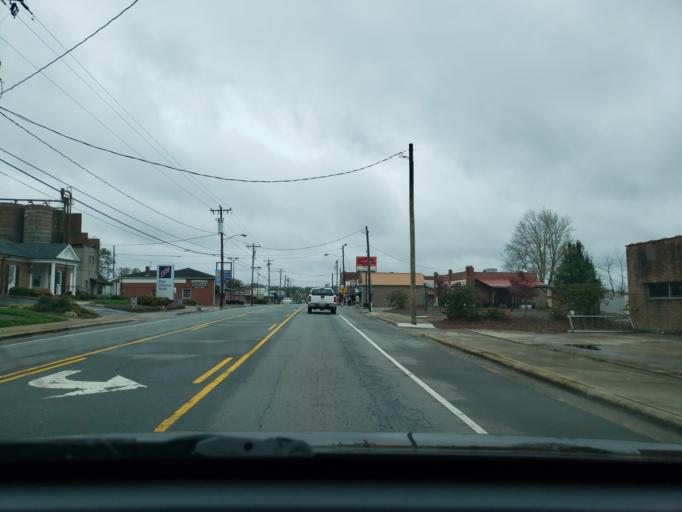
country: US
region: North Carolina
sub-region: Stokes County
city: Walnut Cove
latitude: 36.2981
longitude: -80.1417
